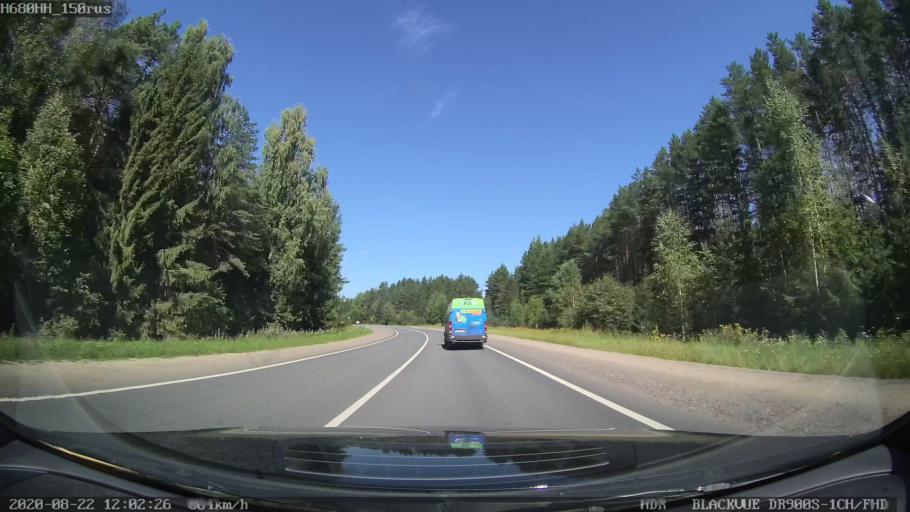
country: RU
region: Tverskaya
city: Rameshki
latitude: 57.2423
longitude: 36.0999
